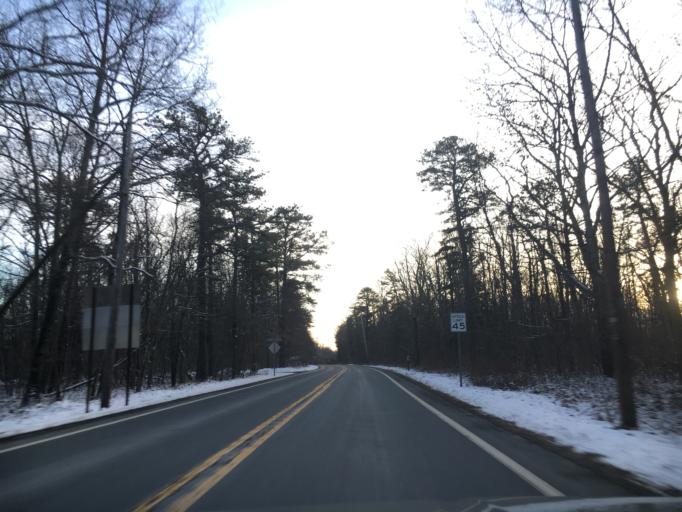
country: US
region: Pennsylvania
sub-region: Pike County
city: Hemlock Farms
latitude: 41.2326
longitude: -75.0747
